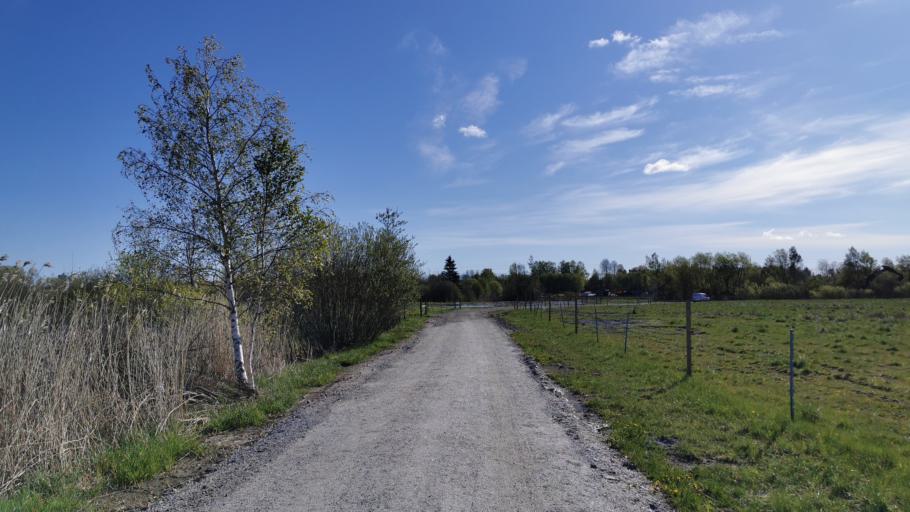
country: SE
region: OErebro
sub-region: Orebro Kommun
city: Orebro
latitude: 59.3065
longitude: 15.2177
